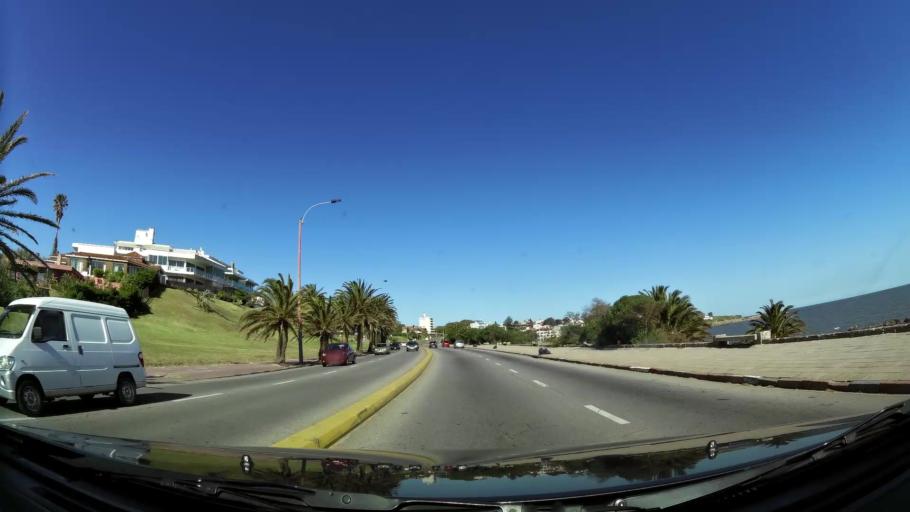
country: UY
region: Canelones
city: Paso de Carrasco
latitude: -34.8954
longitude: -56.0880
